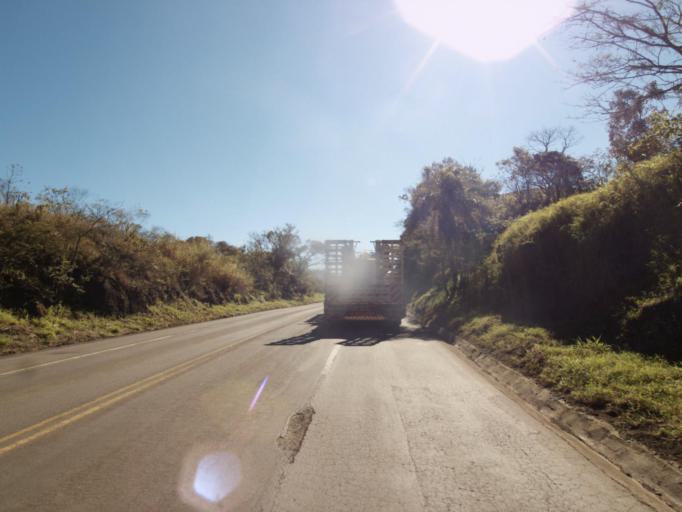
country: BR
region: Rio Grande do Sul
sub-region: Frederico Westphalen
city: Frederico Westphalen
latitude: -26.8196
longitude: -53.4276
